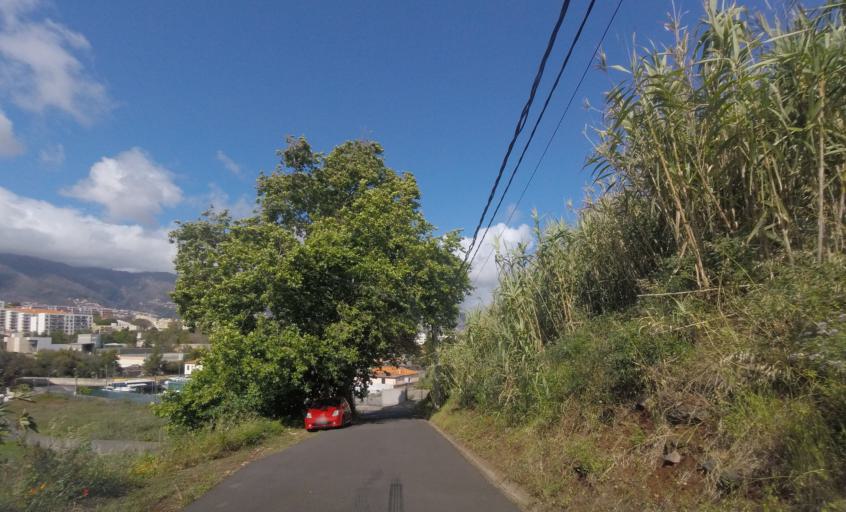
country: PT
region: Madeira
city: Camara de Lobos
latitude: 32.6438
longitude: -16.9403
